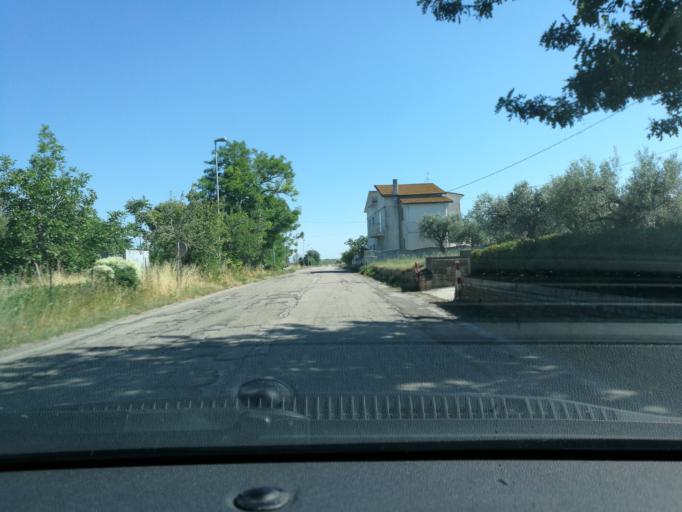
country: IT
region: Abruzzo
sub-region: Provincia di Chieti
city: Vasto
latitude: 42.1647
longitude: 14.7027
